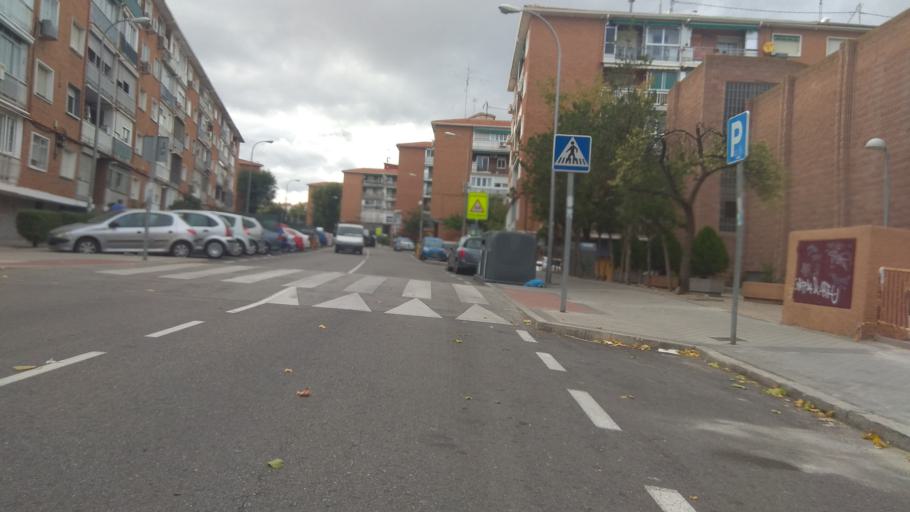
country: ES
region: Madrid
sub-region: Provincia de Madrid
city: Vicalvaro
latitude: 40.4070
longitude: -3.6062
